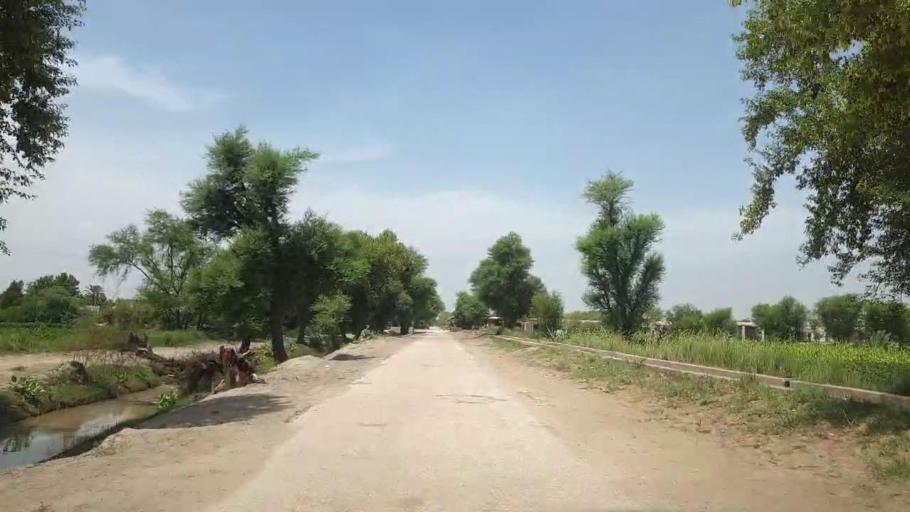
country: PK
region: Sindh
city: Kot Diji
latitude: 27.1351
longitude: 69.0295
